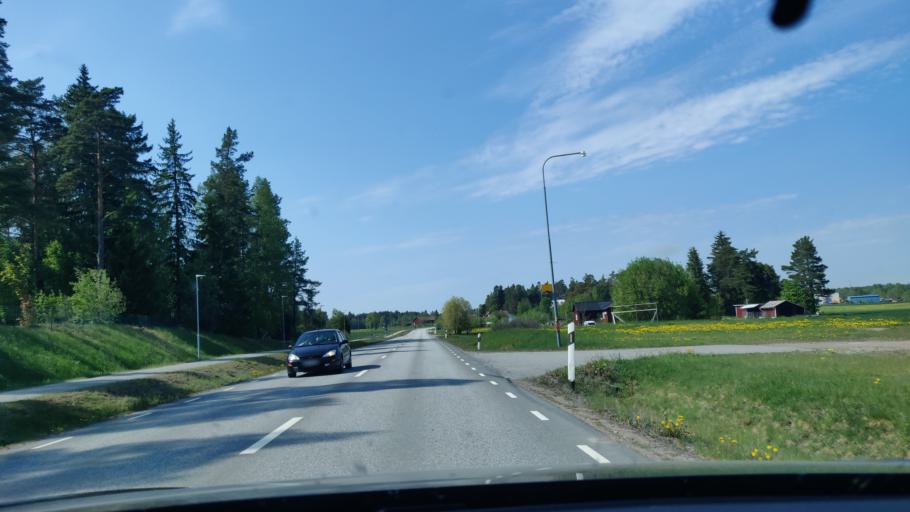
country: SE
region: Uppsala
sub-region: Heby Kommun
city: OEstervala
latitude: 60.1702
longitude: 17.1866
